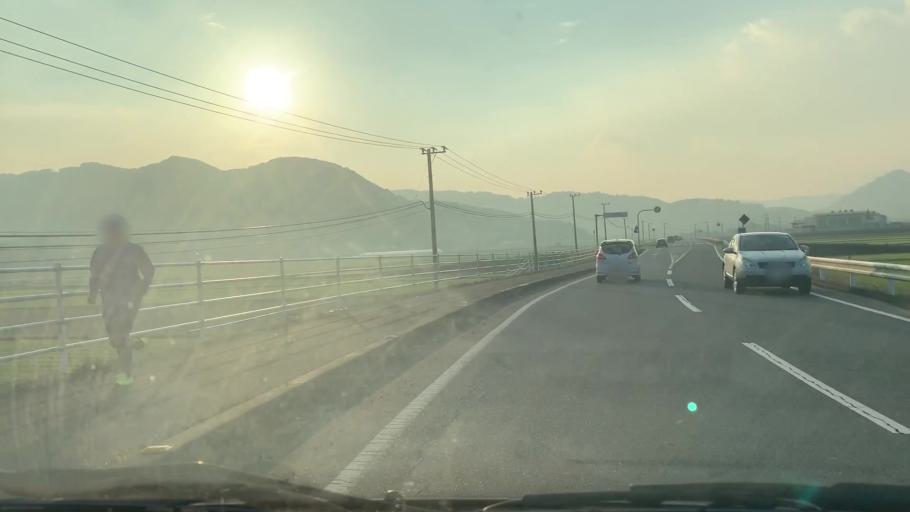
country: JP
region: Saga Prefecture
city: Takeocho-takeo
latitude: 33.2721
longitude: 130.1386
